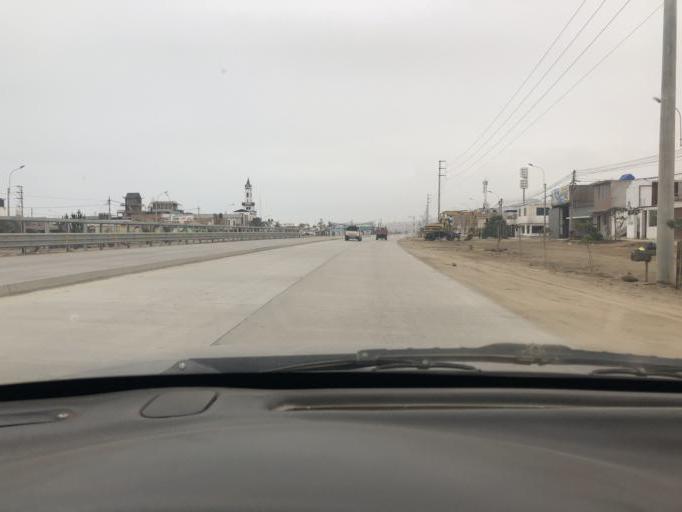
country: PE
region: Lima
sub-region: Lima
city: San Bartolo
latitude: -12.3687
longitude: -76.7916
